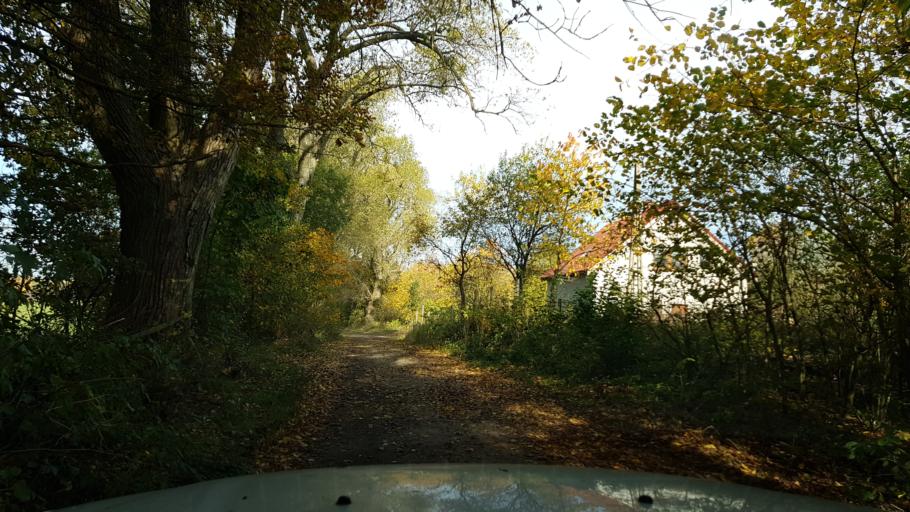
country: PL
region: West Pomeranian Voivodeship
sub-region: Powiat swidwinski
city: Polczyn-Zdroj
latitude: 53.7610
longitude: 16.0295
